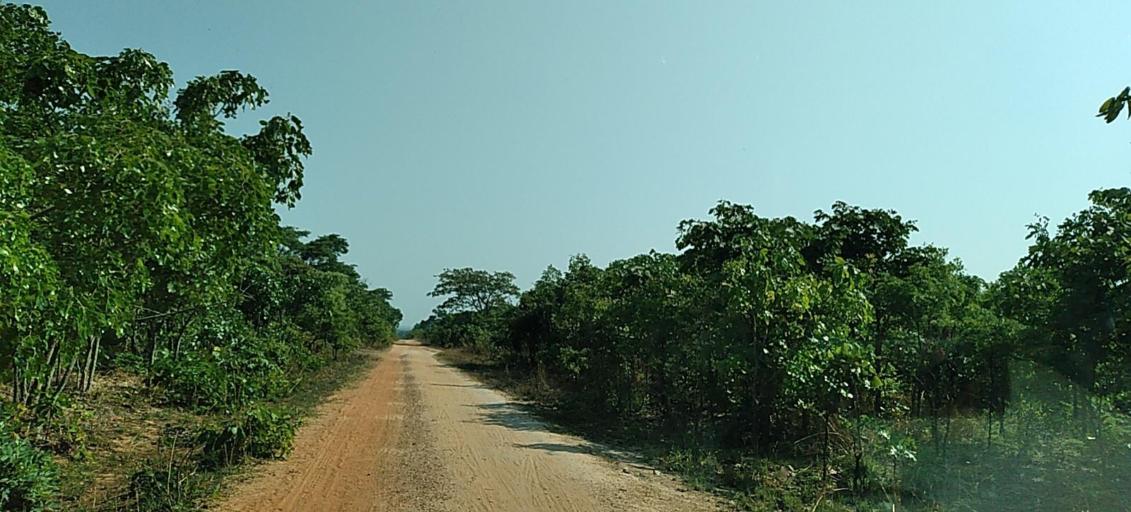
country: ZM
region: Copperbelt
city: Luanshya
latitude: -13.2938
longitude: 28.2506
